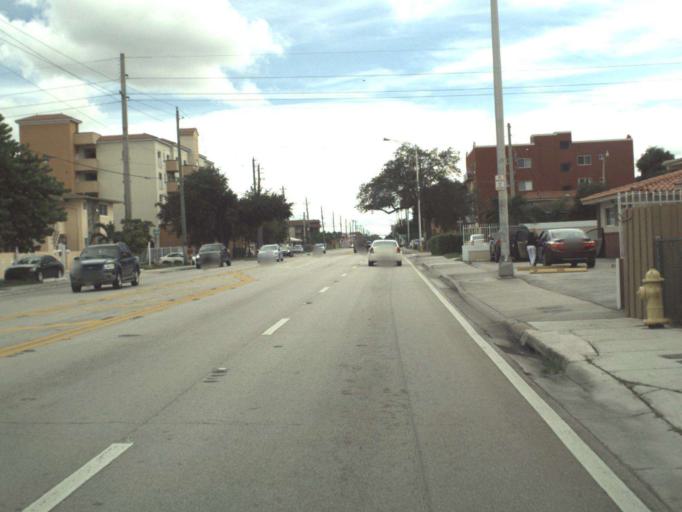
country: US
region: Florida
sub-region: Miami-Dade County
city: West Miami
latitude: 25.7753
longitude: -80.2883
